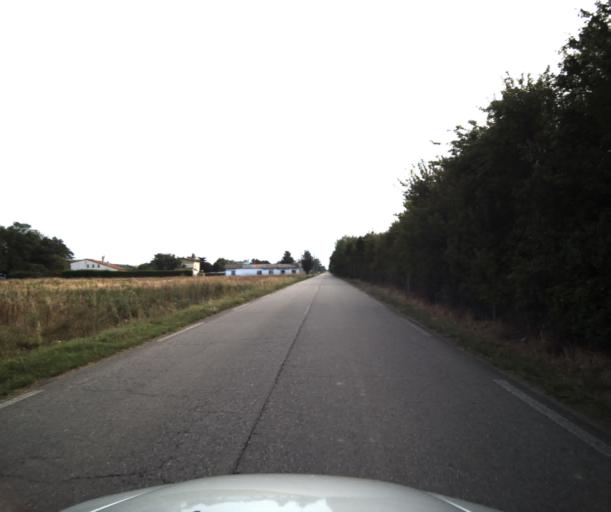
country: FR
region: Midi-Pyrenees
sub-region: Departement de la Haute-Garonne
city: Le Fauga
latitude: 43.4288
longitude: 1.3066
